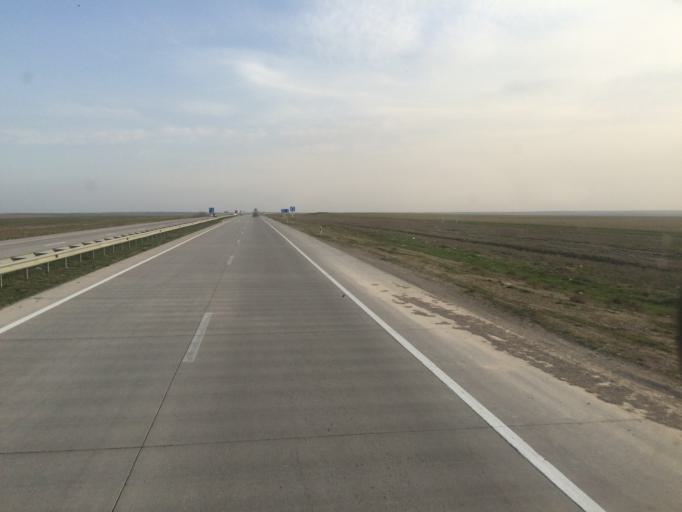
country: KZ
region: Ongtustik Qazaqstan
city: Temirlanovka
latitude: 42.7378
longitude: 69.2078
